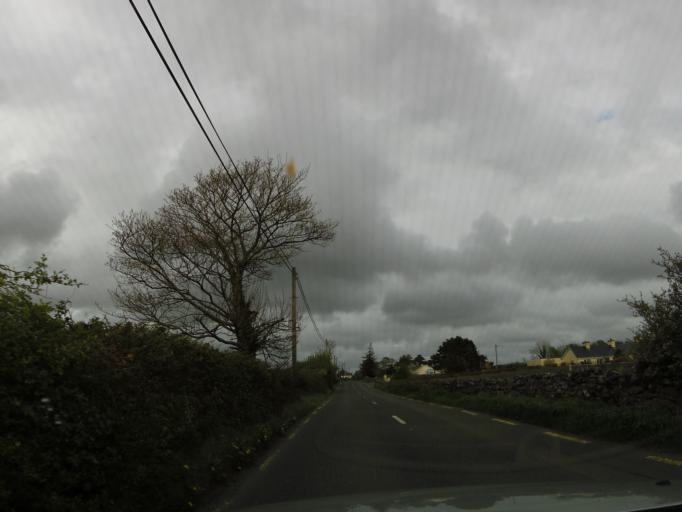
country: IE
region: Connaught
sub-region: Maigh Eo
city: Ballinrobe
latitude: 53.6367
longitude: -9.1865
